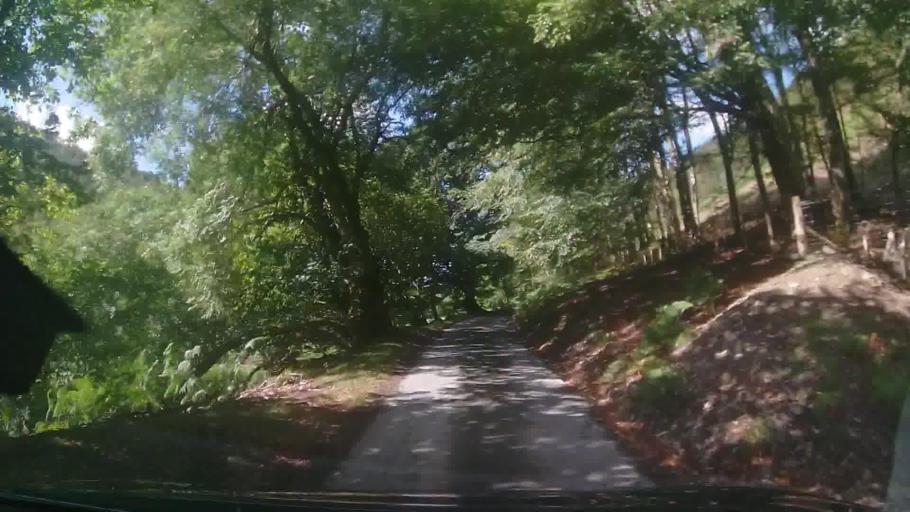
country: GB
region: Wales
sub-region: Gwynedd
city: Bala
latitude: 52.7903
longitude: -3.5420
